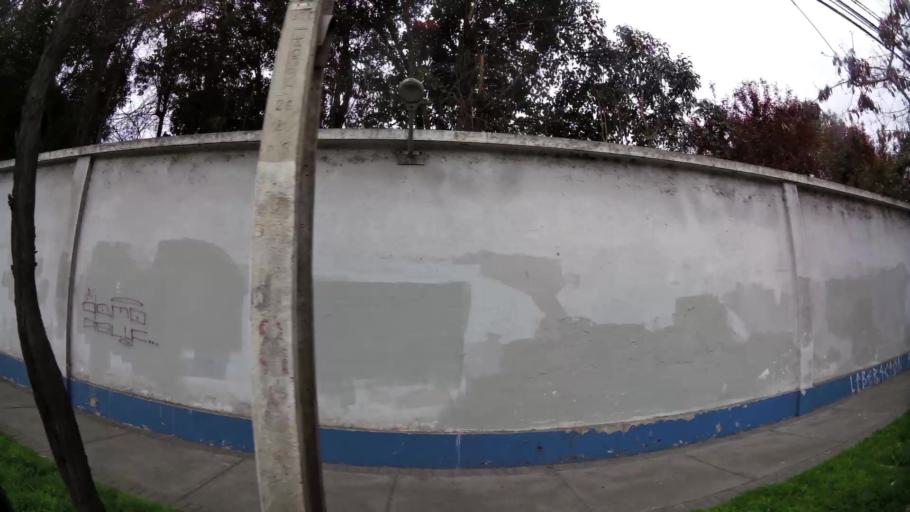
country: CL
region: Santiago Metropolitan
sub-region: Provincia de Santiago
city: Lo Prado
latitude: -33.5204
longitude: -70.7555
